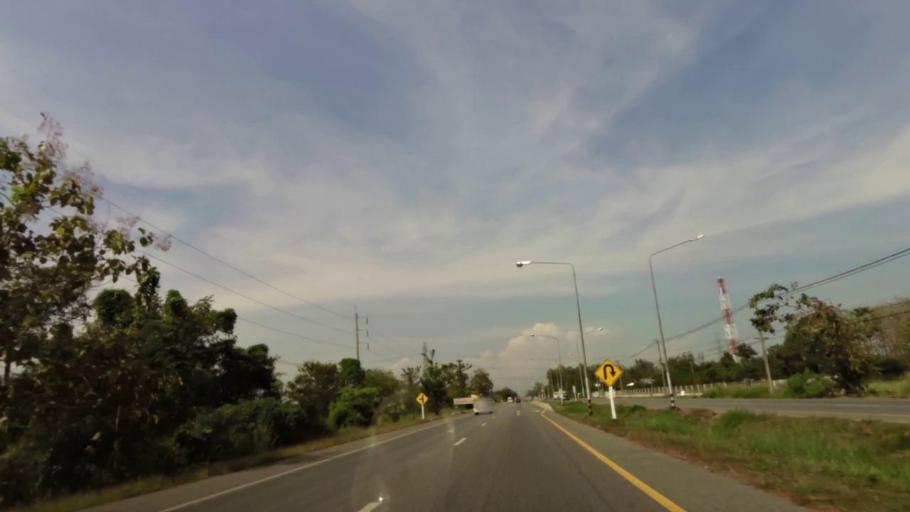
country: TH
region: Uttaradit
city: Tron
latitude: 17.5436
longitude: 100.1919
